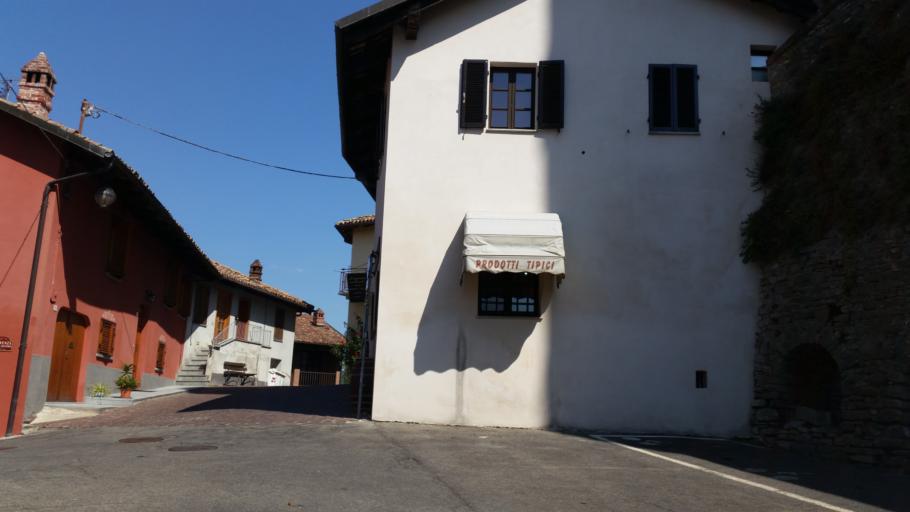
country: IT
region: Piedmont
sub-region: Provincia di Cuneo
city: Serralunga d'Alba
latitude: 44.6110
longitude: 8.0002
